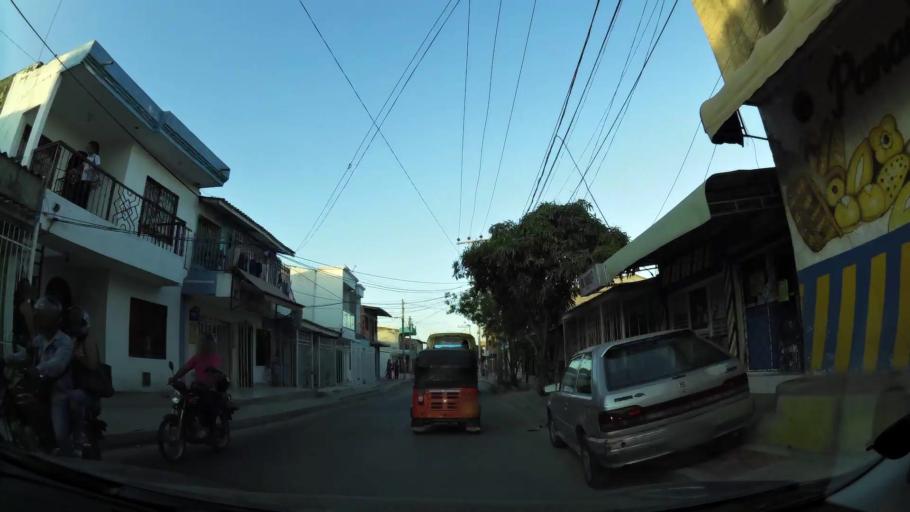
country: CO
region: Atlantico
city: Soledad
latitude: 10.9215
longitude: -74.7879
